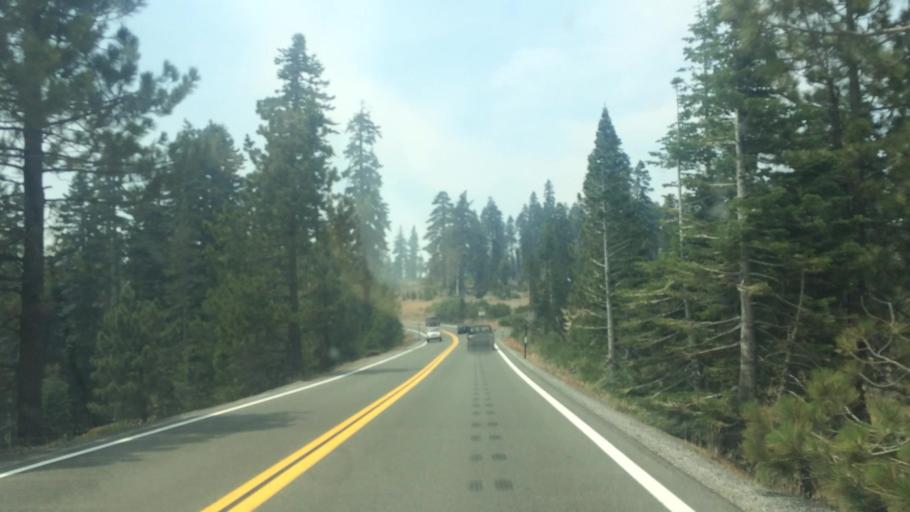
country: US
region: California
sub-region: Calaveras County
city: Arnold
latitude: 38.5847
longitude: -120.2489
